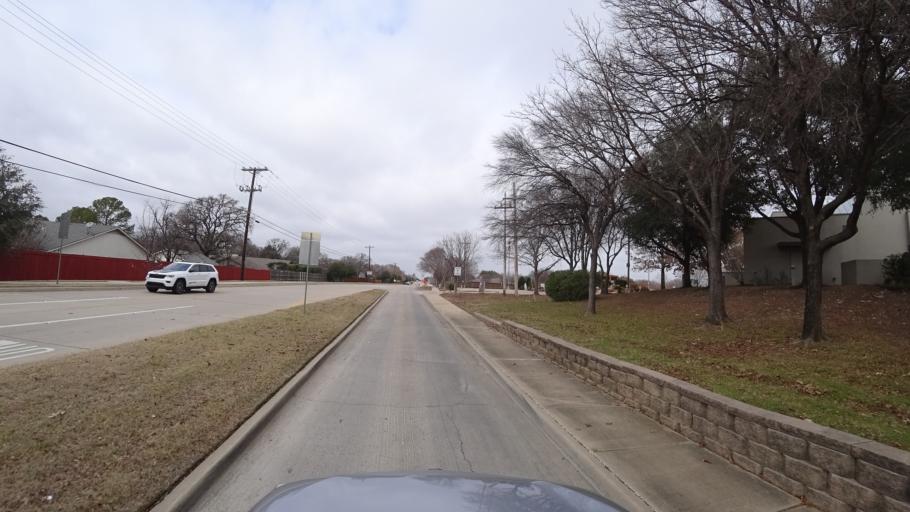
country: US
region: Texas
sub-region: Denton County
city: Highland Village
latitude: 33.0427
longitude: -97.0446
